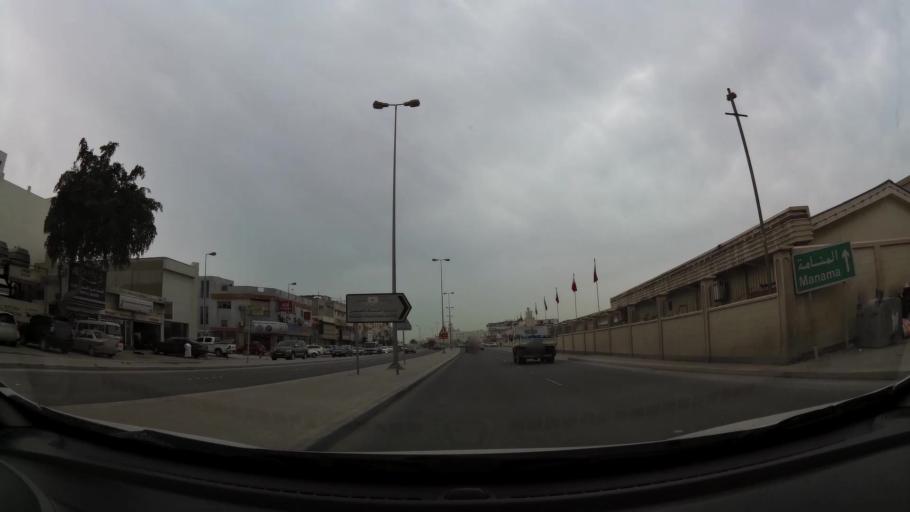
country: BH
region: Northern
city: Madinat `Isa
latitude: 26.1864
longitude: 50.5294
